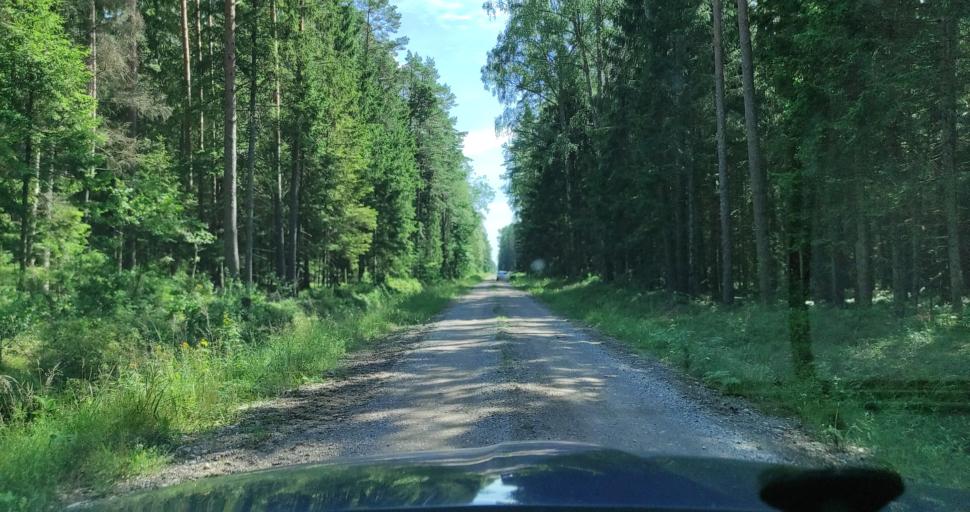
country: LV
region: Pavilostas
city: Pavilosta
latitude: 56.7922
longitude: 21.2778
